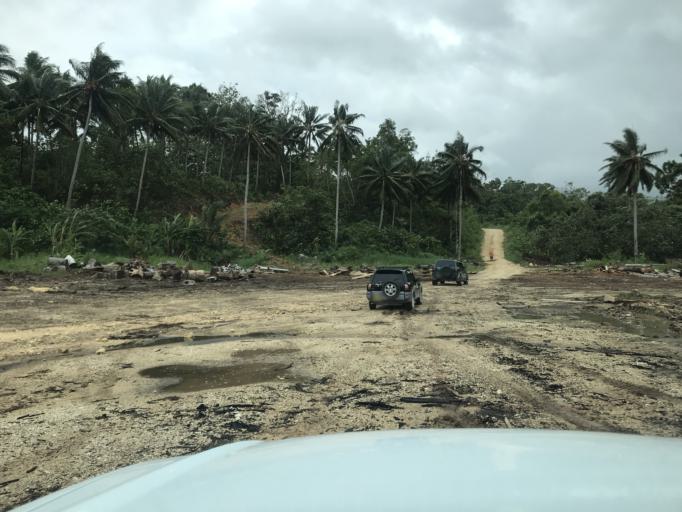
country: SB
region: Malaita
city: Auki
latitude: -8.6318
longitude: 160.6599
